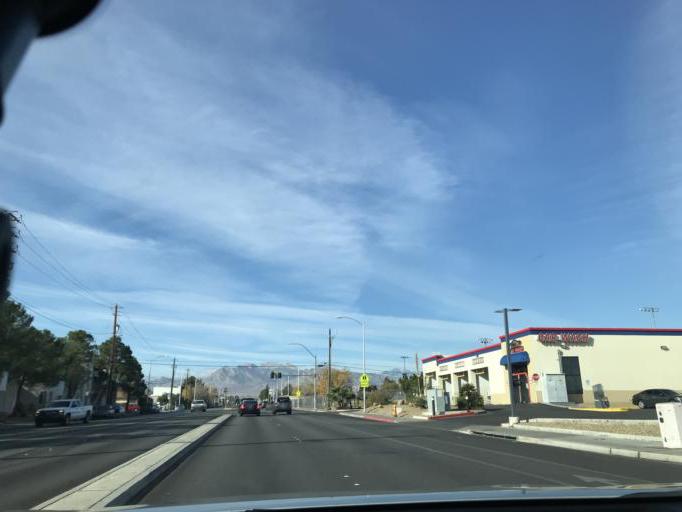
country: US
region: Nevada
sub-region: Clark County
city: Las Vegas
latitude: 36.2031
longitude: -115.2239
